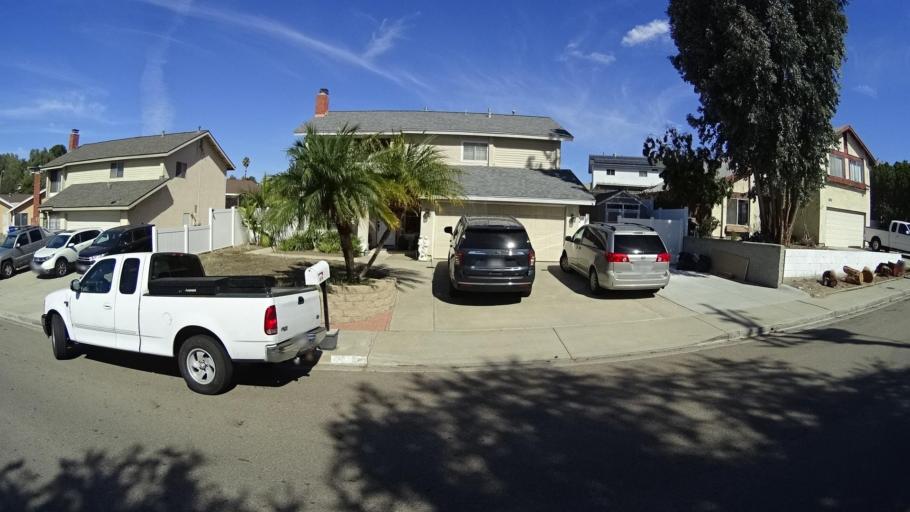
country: US
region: California
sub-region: San Diego County
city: Lemon Grove
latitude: 32.7249
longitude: -117.0198
